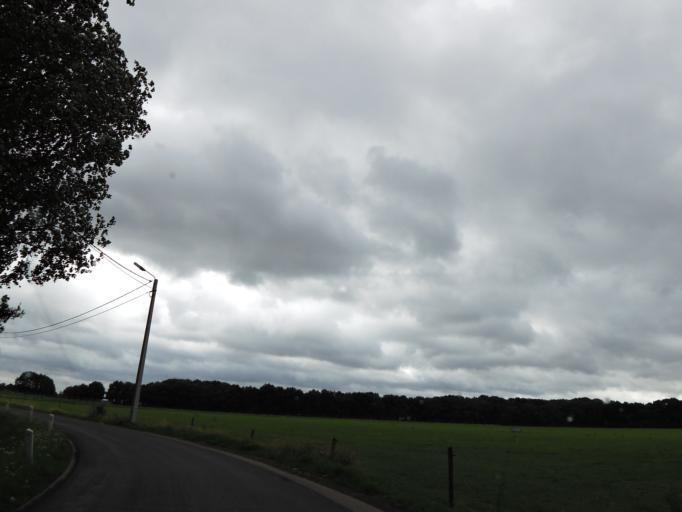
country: BE
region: Flanders
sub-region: Provincie Limburg
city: Maaseik
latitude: 51.0919
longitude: 5.7617
